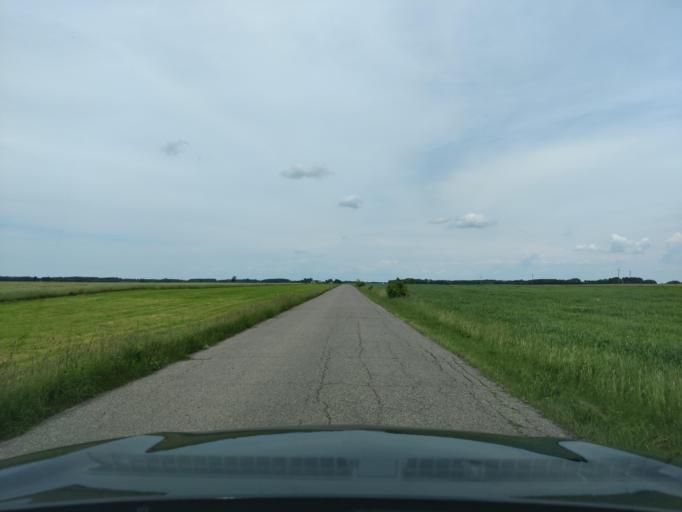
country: PL
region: Masovian Voivodeship
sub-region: Powiat pultuski
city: Obryte
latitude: 52.7184
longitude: 21.2397
